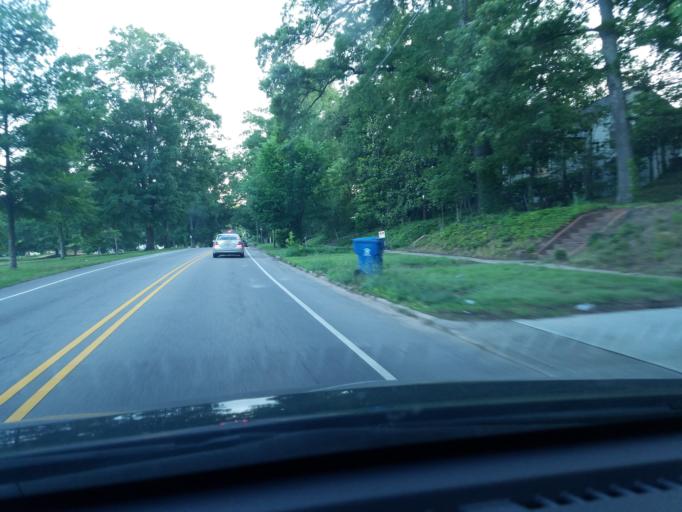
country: US
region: North Carolina
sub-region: Durham County
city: Durham
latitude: 35.9819
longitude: -78.9128
